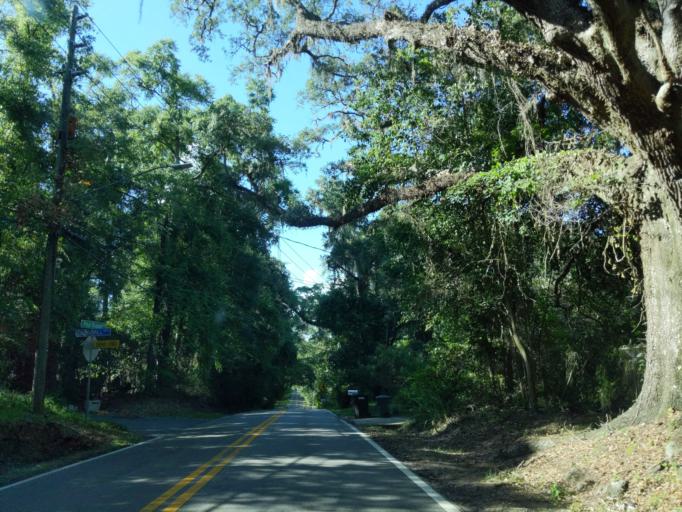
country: US
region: Florida
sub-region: Leon County
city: Tallahassee
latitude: 30.4135
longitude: -84.2437
